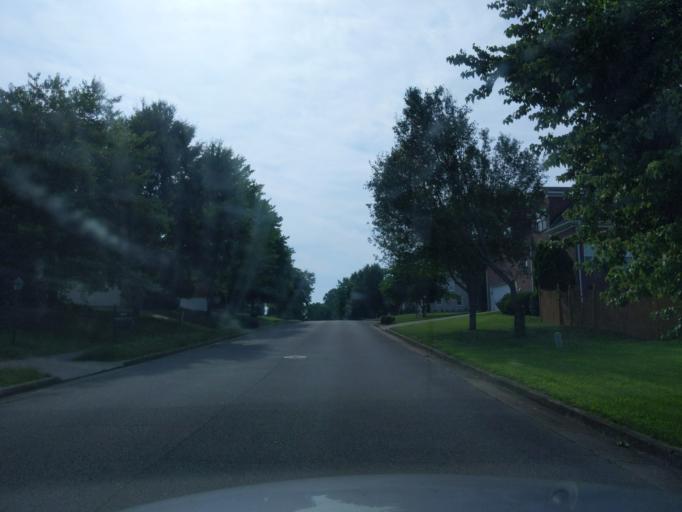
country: US
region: Tennessee
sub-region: Williamson County
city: Brentwood Estates
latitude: 36.0250
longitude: -86.7456
